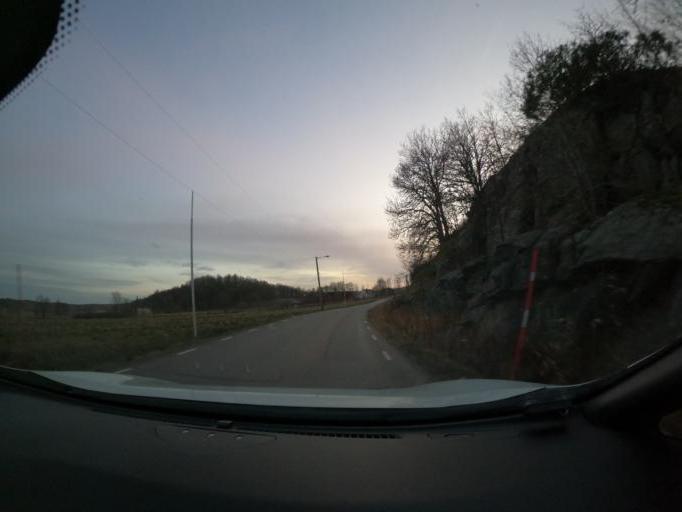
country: SE
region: Vaestra Goetaland
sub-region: Harryda Kommun
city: Molnlycke
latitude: 57.6044
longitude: 12.1359
